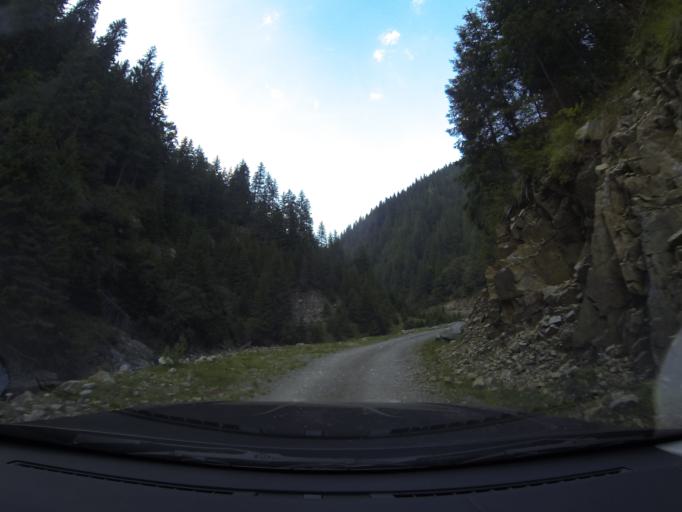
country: RO
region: Brasov
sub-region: Oras Victoria
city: Victoria
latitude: 45.5464
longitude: 24.6792
